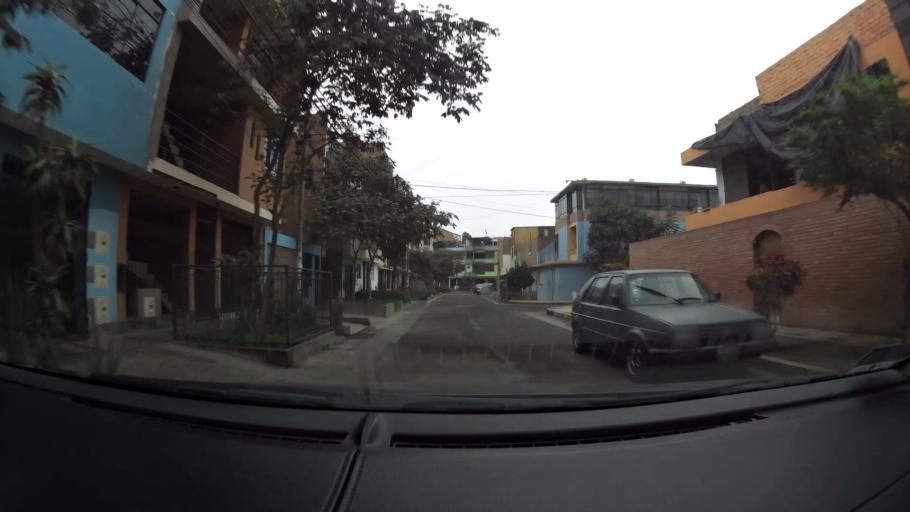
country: PE
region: Lima
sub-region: Lima
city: Independencia
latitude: -11.9756
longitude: -77.0730
